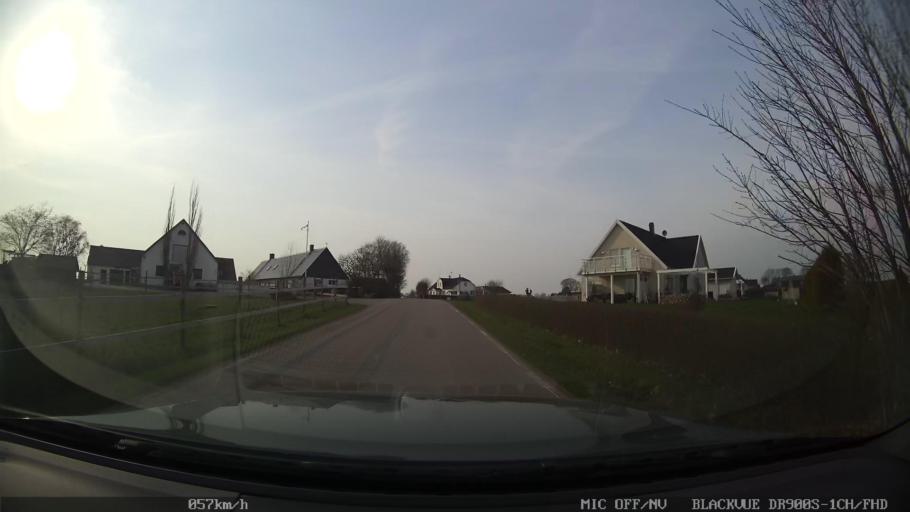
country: SE
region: Skane
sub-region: Ystads Kommun
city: Ystad
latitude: 55.4664
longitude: 13.8136
